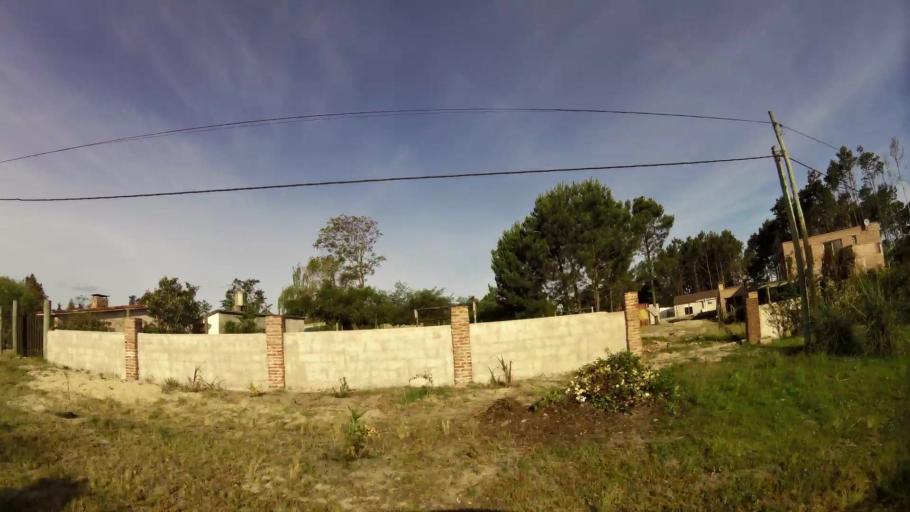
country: UY
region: Canelones
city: Empalme Olmos
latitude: -34.7863
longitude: -55.8595
